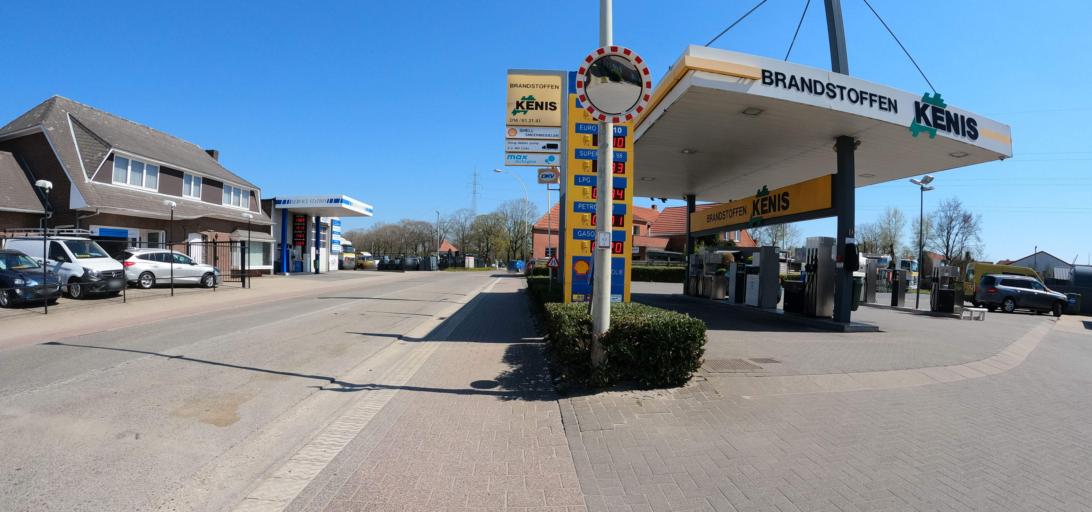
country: BE
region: Flanders
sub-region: Provincie Antwerpen
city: Beerse
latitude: 51.3253
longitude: 4.8312
